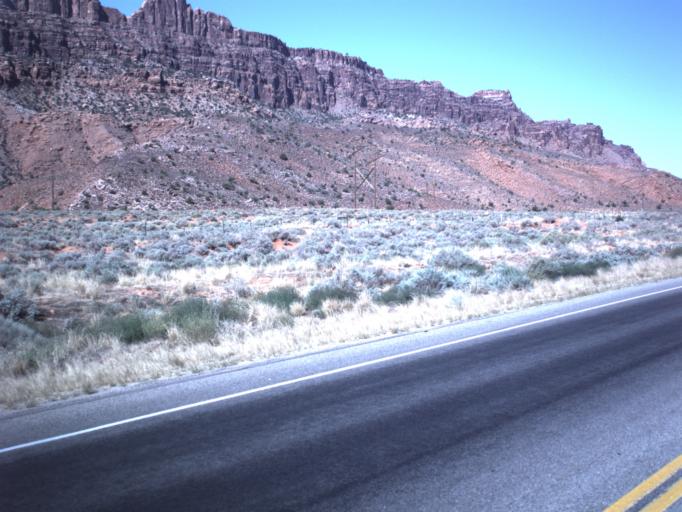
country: US
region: Utah
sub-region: Grand County
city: Moab
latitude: 38.5102
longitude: -109.4854
